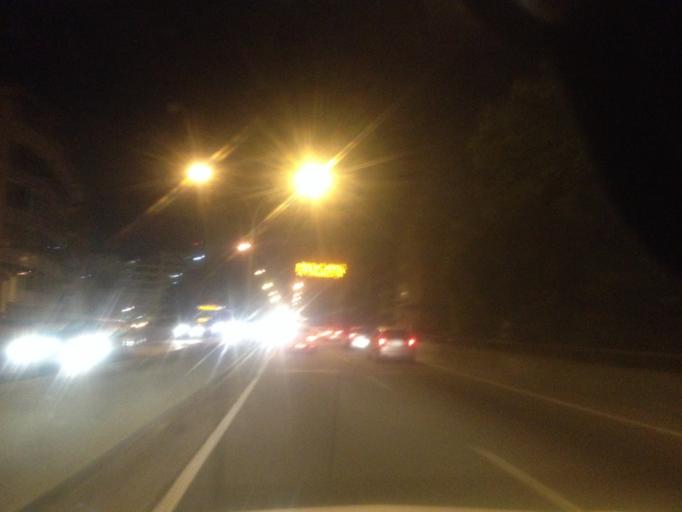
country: BR
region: Rio de Janeiro
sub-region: Rio De Janeiro
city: Rio de Janeiro
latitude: -22.9193
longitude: -43.2099
